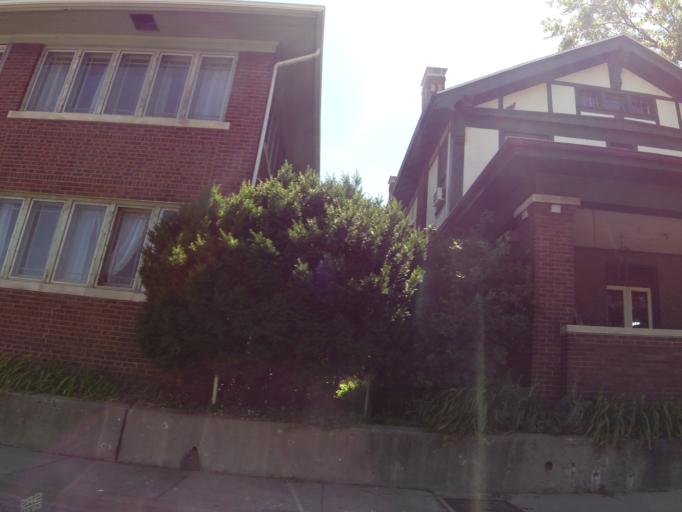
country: US
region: Illinois
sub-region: Vermilion County
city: Danville
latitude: 40.1278
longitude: -87.6356
